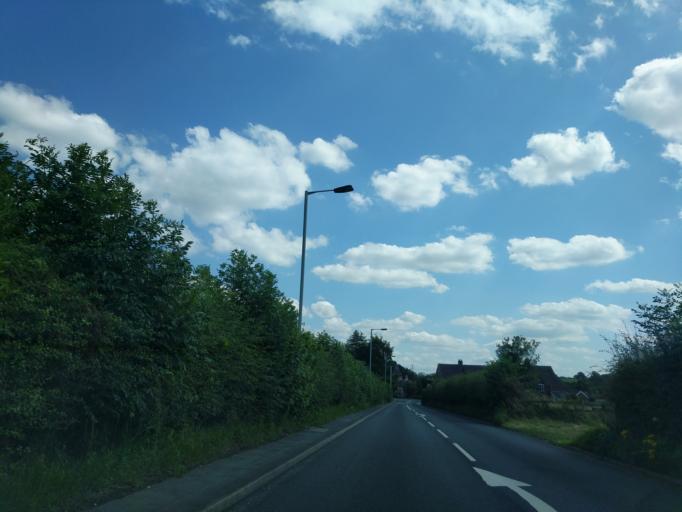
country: GB
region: England
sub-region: Staffordshire
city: Cheadle
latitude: 52.9465
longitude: -1.9796
